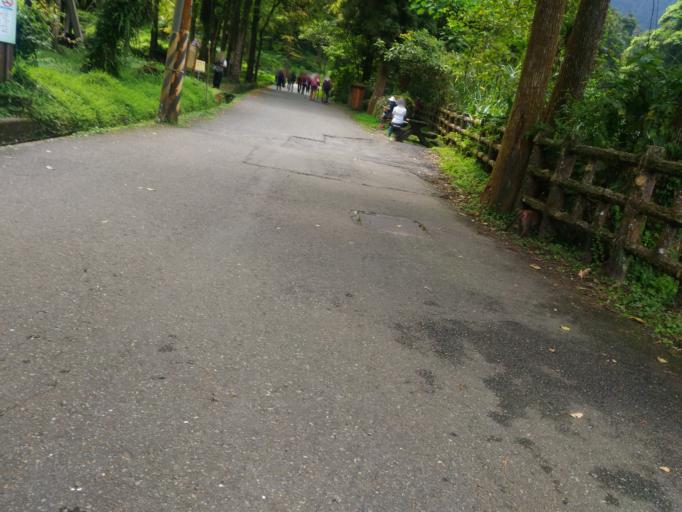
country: TW
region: Taiwan
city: Lugu
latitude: 23.6674
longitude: 120.7981
